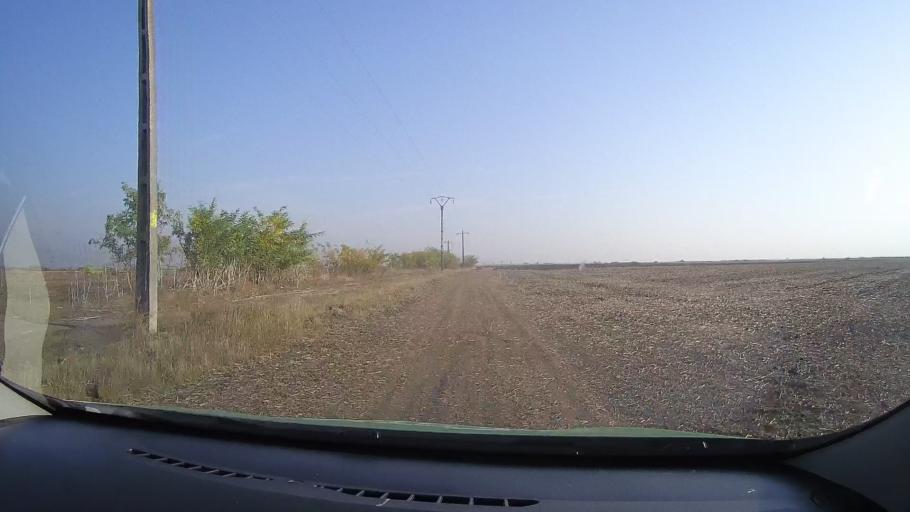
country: RO
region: Arad
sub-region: Comuna Graniceri
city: Graniceri
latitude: 46.5387
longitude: 21.3255
